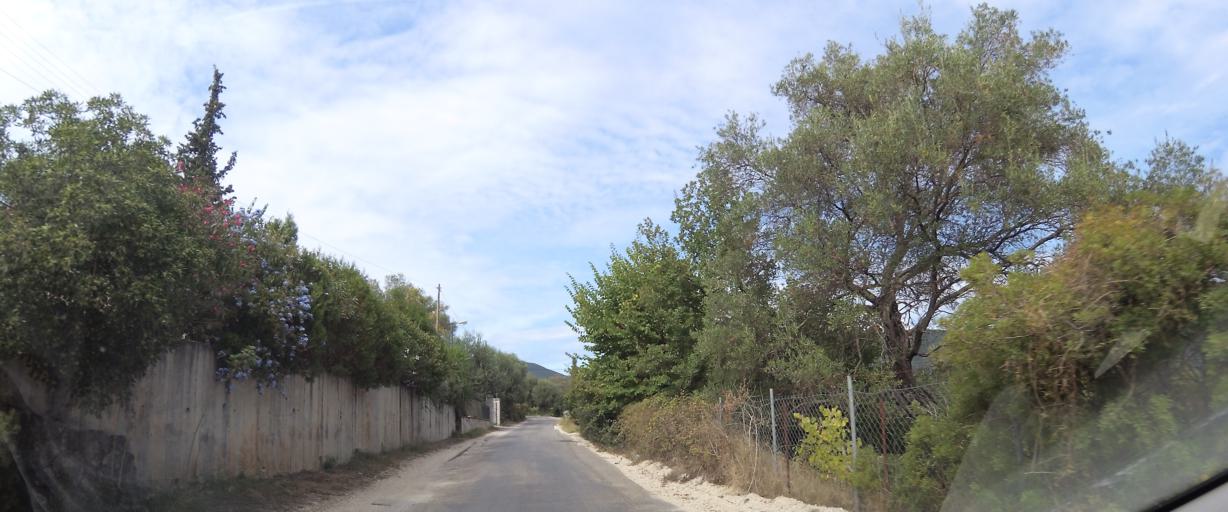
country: GR
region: Ionian Islands
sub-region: Nomos Kerkyras
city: Kontokali
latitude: 39.6911
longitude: 19.8154
